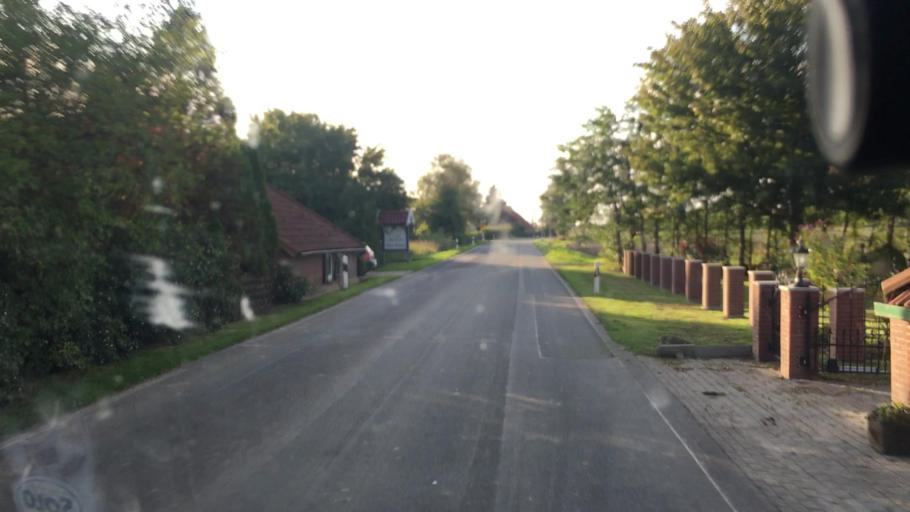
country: DE
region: Lower Saxony
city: Werdum
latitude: 53.6555
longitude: 7.7785
